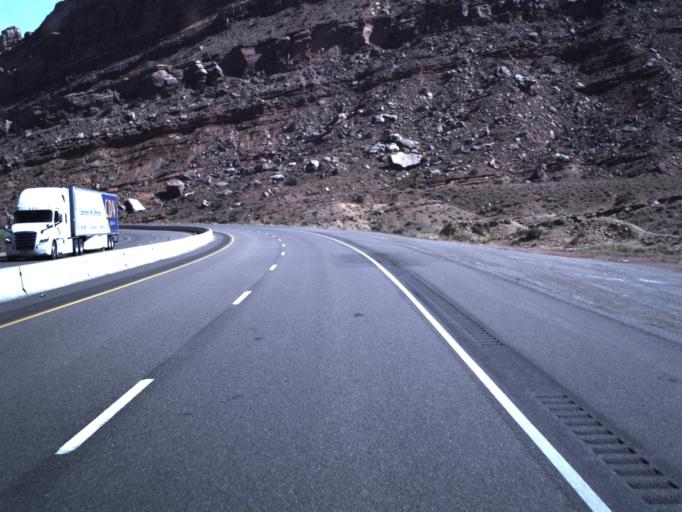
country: US
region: Utah
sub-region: Carbon County
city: East Carbon City
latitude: 38.9259
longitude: -110.4536
